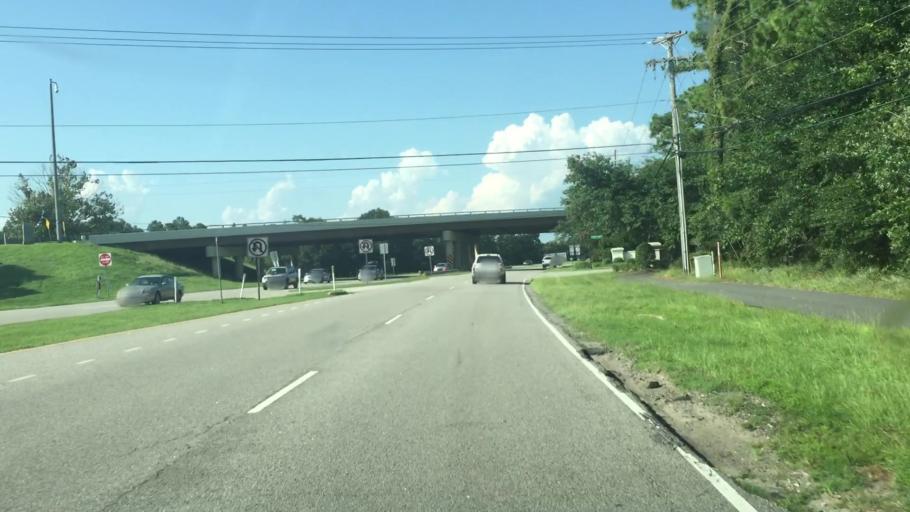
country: US
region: South Carolina
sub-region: Horry County
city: Myrtle Beach
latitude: 33.7663
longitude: -78.8055
